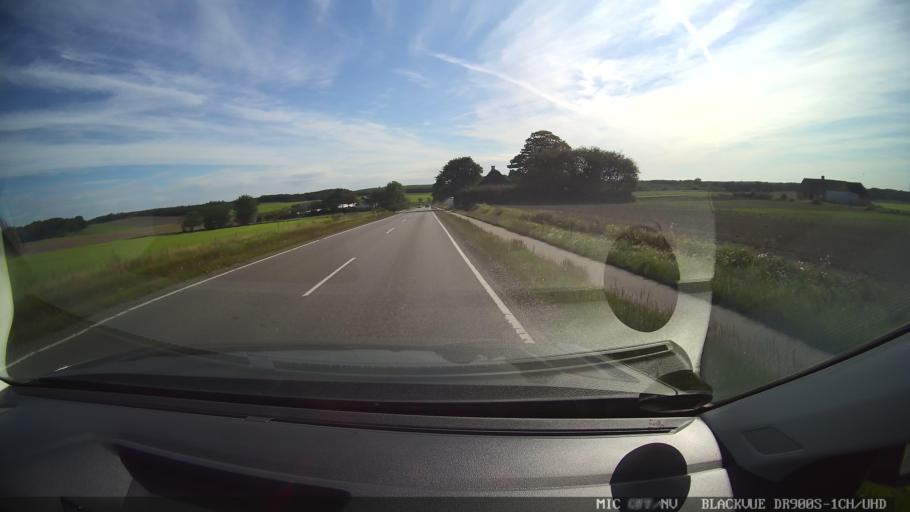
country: DK
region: North Denmark
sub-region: Mariagerfjord Kommune
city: Arden
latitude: 56.7740
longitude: 9.8300
